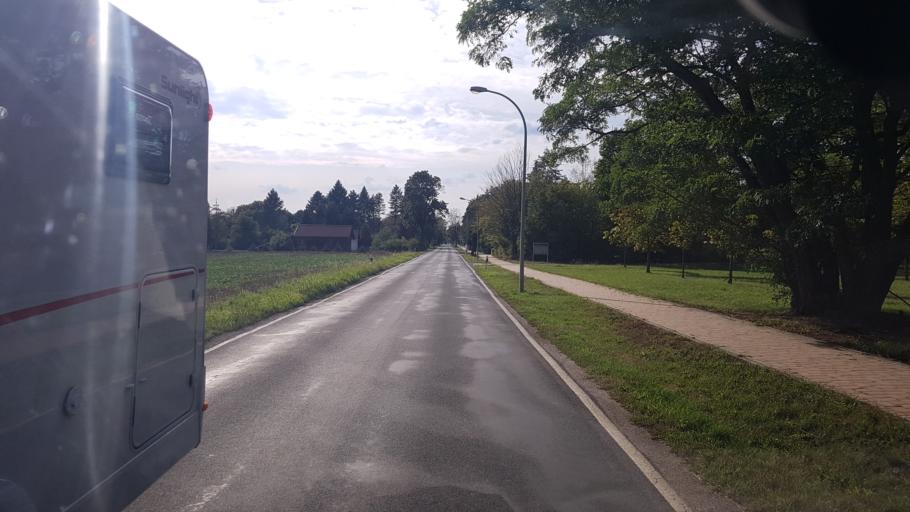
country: DE
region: Brandenburg
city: Welzow
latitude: 51.5506
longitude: 14.2144
